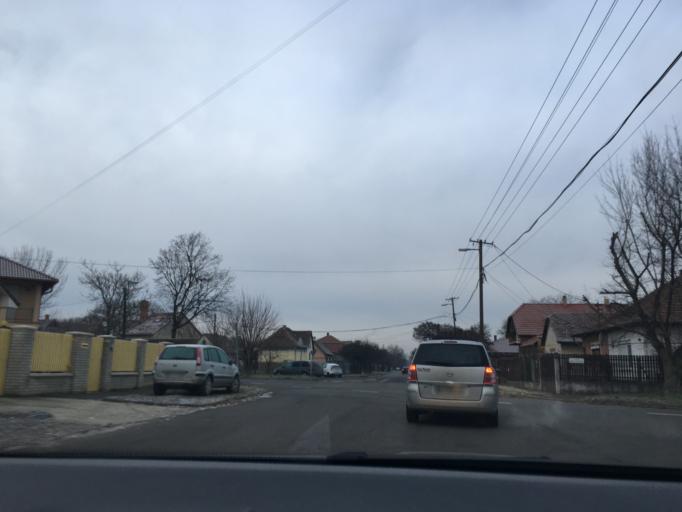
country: HU
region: Hajdu-Bihar
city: Debrecen
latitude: 47.5390
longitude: 21.6548
